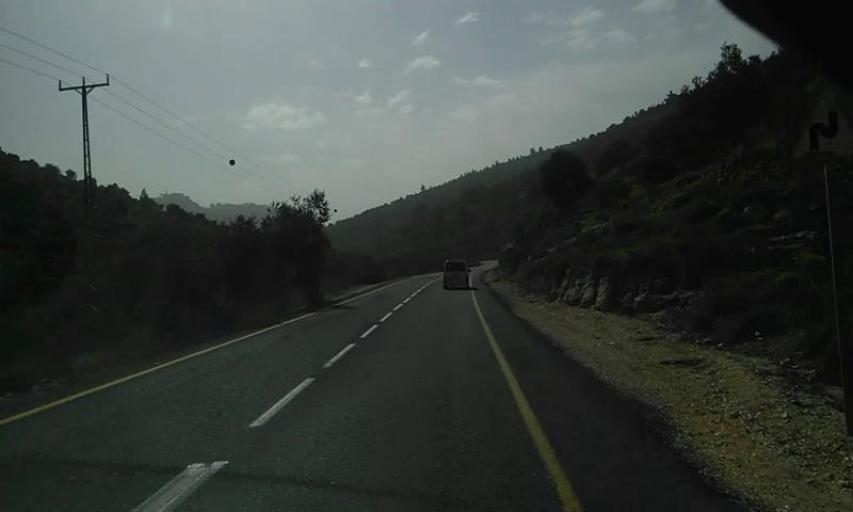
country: PS
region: West Bank
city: Silwad
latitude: 31.9968
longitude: 35.2403
